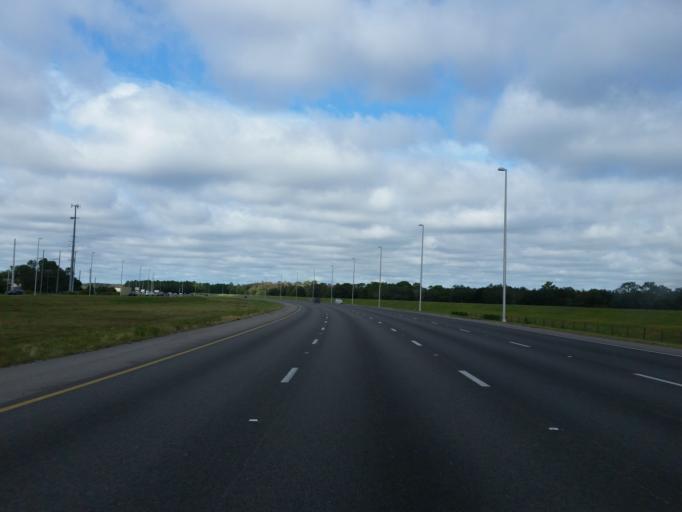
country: US
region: Florida
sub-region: Hillsborough County
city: Pebble Creek
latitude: 28.0901
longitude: -82.3546
